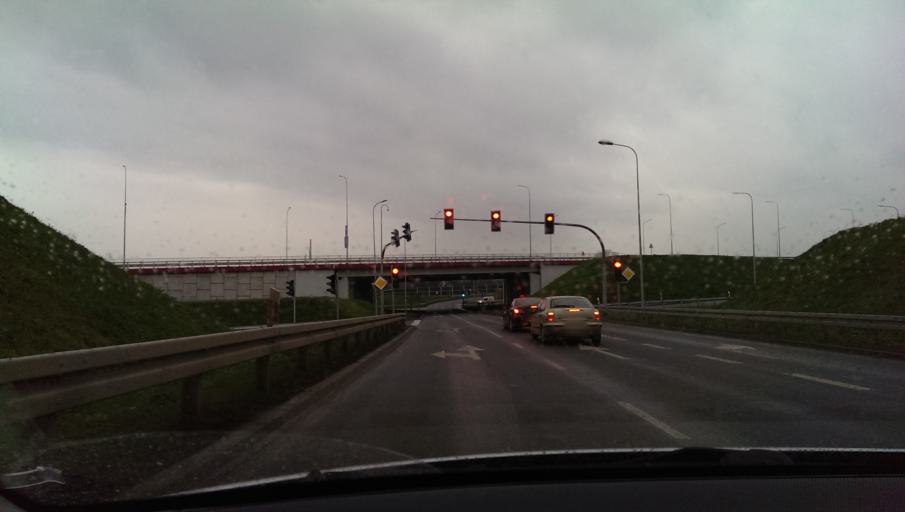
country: PL
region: Lesser Poland Voivodeship
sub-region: Powiat wielicki
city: Kokotow
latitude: 50.0644
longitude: 20.0745
